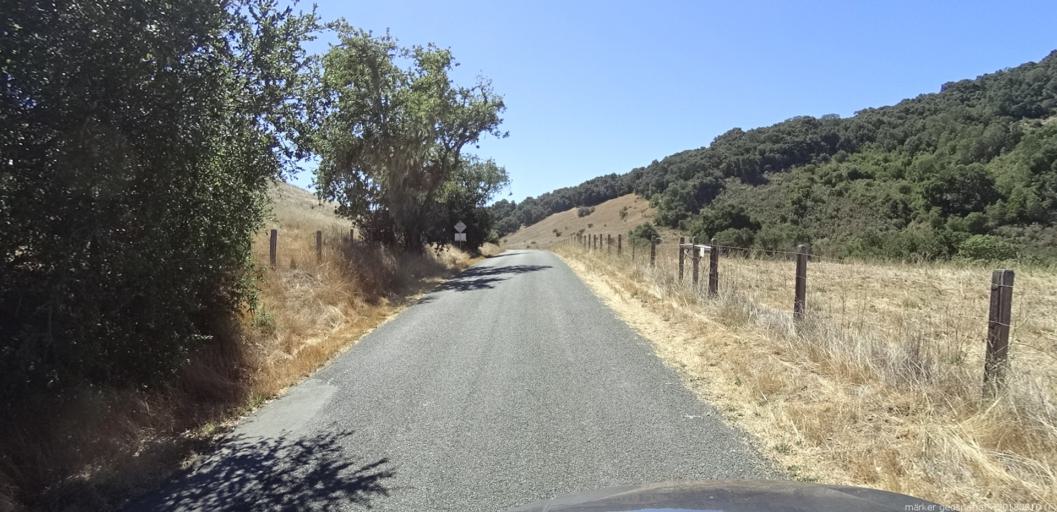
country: US
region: California
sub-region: Monterey County
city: Carmel Valley Village
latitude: 36.4727
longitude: -121.8019
